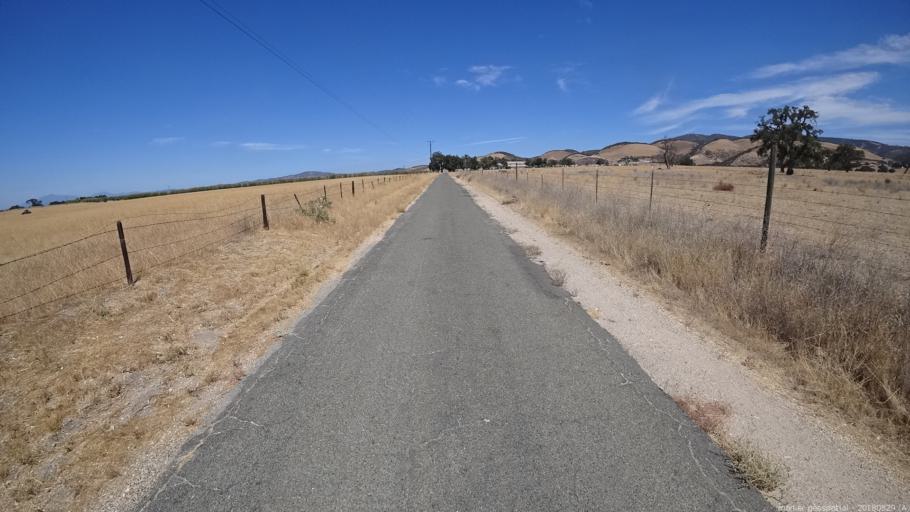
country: US
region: California
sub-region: San Luis Obispo County
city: Lake Nacimiento
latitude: 35.9118
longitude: -121.0379
